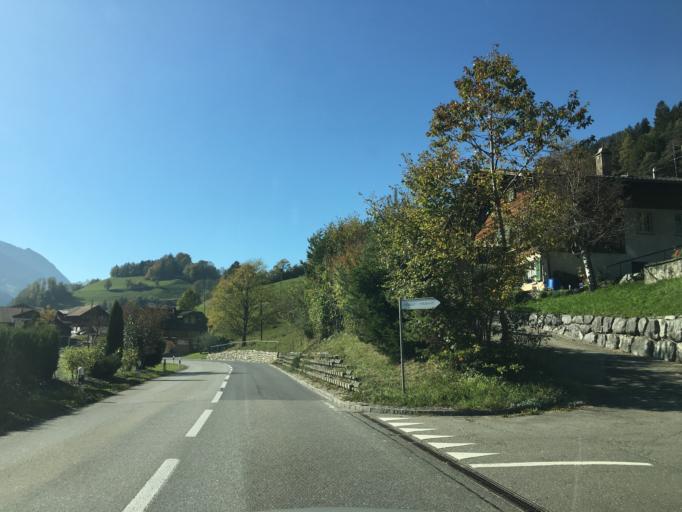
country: CH
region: Bern
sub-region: Frutigen-Niedersimmental District
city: Diemtigen
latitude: 46.6671
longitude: 7.5857
